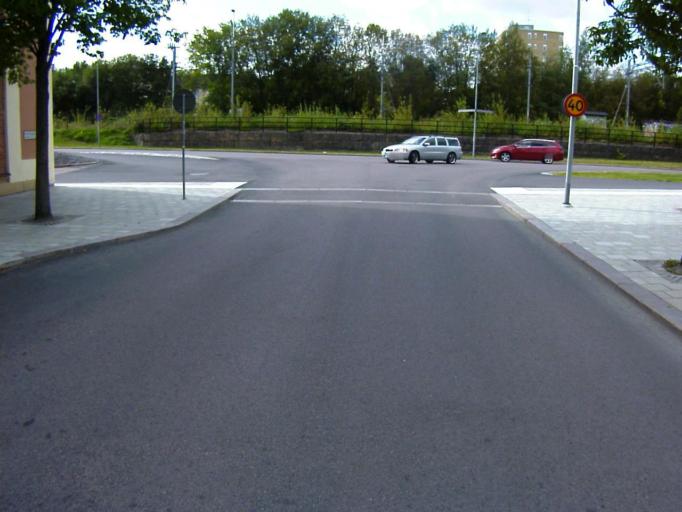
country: SE
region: Soedermanland
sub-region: Eskilstuna Kommun
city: Eskilstuna
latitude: 59.3688
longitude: 16.5109
